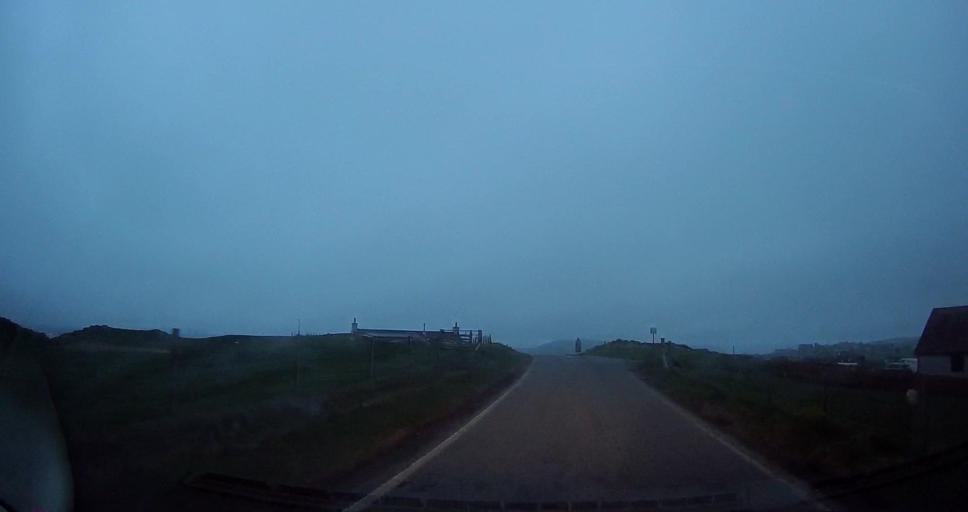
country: GB
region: Scotland
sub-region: Shetland Islands
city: Sandwick
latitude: 60.0145
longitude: -1.2276
